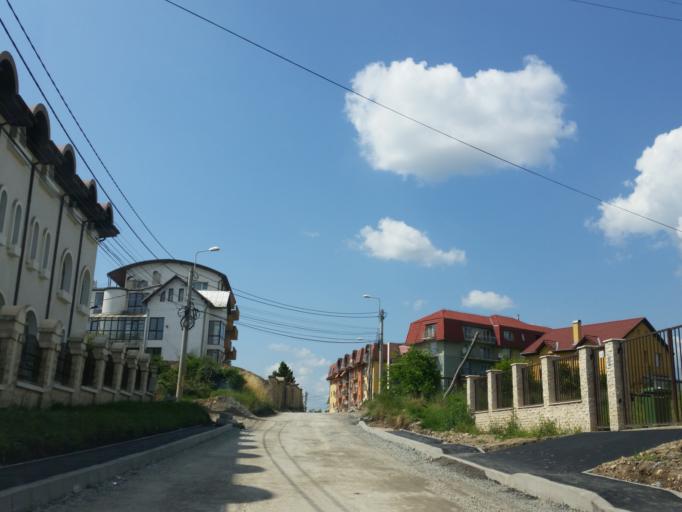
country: RO
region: Cluj
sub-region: Municipiul Cluj-Napoca
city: Cluj-Napoca
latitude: 46.7553
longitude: 23.6208
